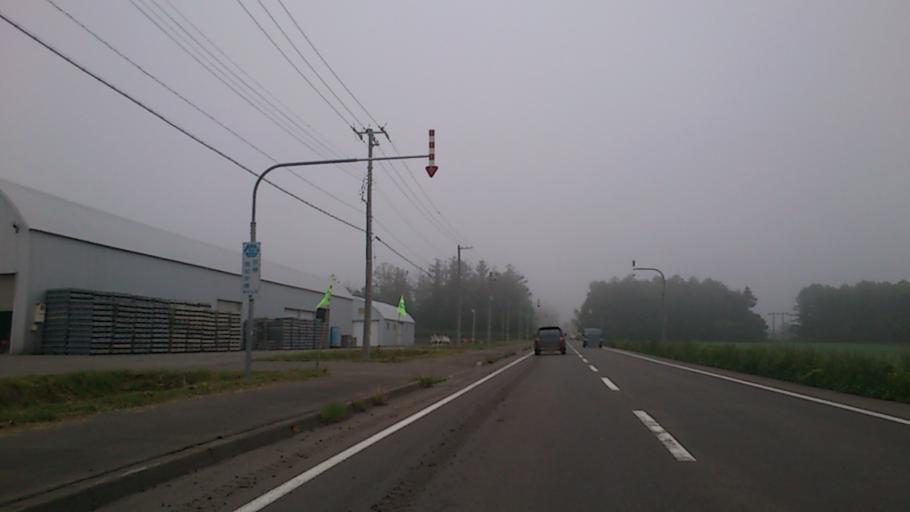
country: JP
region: Hokkaido
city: Niseko Town
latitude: 42.8806
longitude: 140.8191
